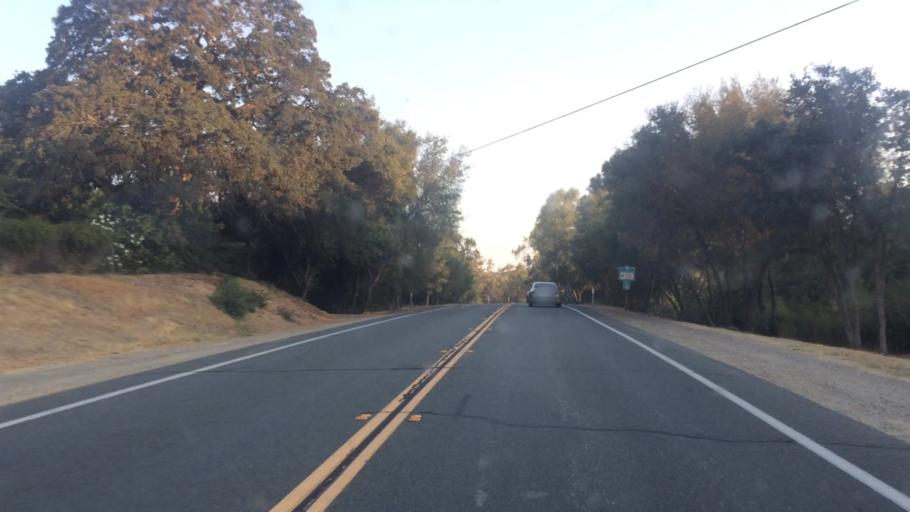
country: US
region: California
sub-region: Amador County
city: Ione
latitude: 38.3593
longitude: -120.9399
